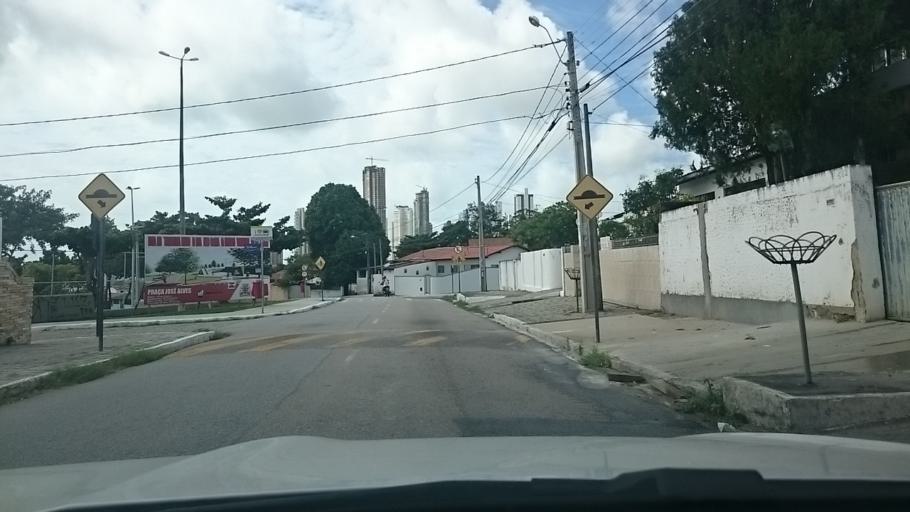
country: BR
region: Paraiba
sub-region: Joao Pessoa
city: Joao Pessoa
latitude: -7.1306
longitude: -34.8400
